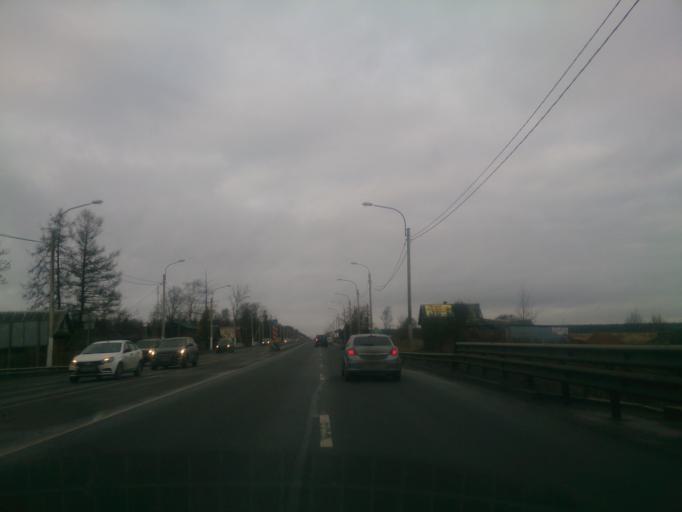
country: RU
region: Leningrad
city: Ul'yanovka
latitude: 59.6191
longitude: 30.7351
